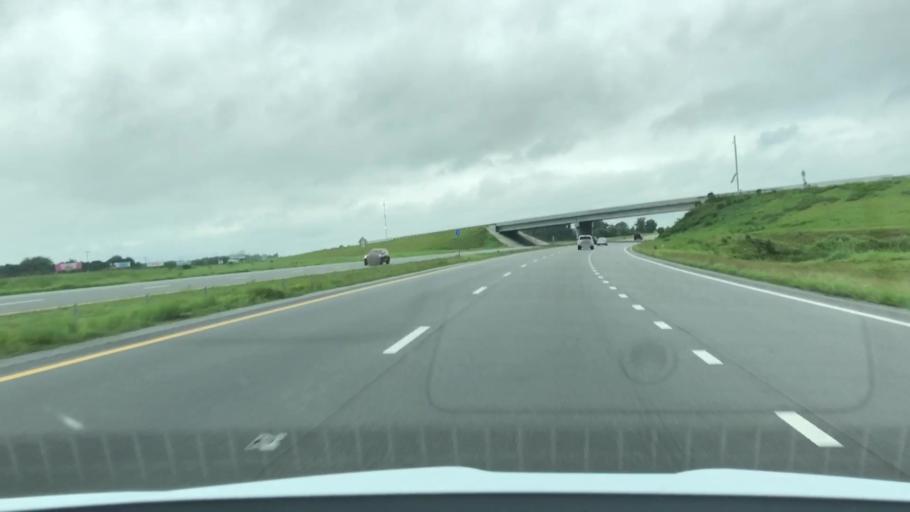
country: US
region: North Carolina
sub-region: Lenoir County
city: La Grange
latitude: 35.3023
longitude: -77.8173
